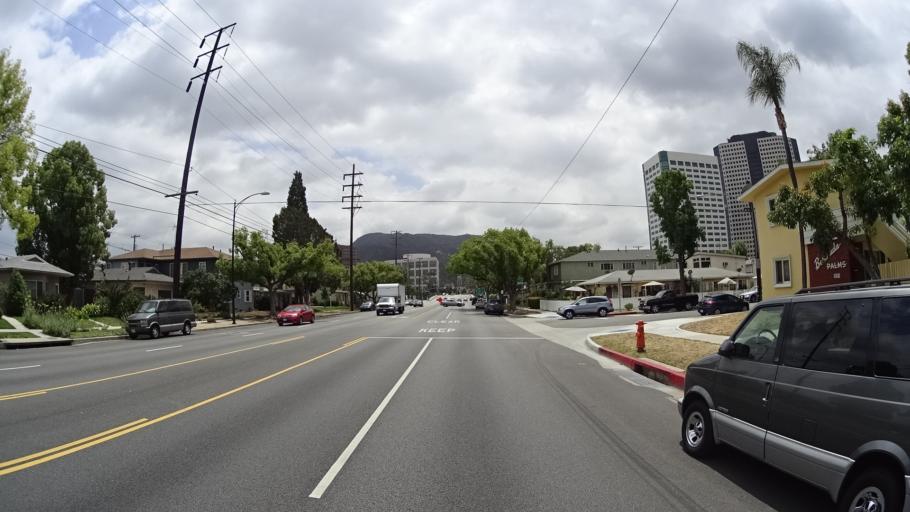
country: US
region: California
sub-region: Los Angeles County
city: Universal City
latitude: 34.1559
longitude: -118.3413
